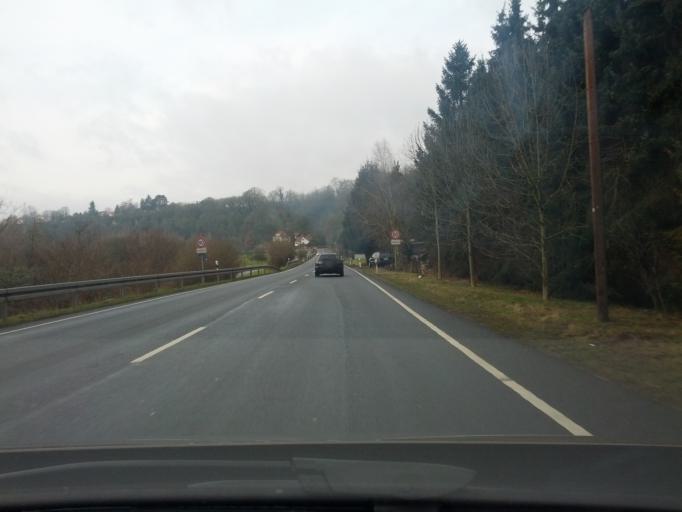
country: DE
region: Hesse
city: Witzenhausen
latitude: 51.3493
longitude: 9.8752
